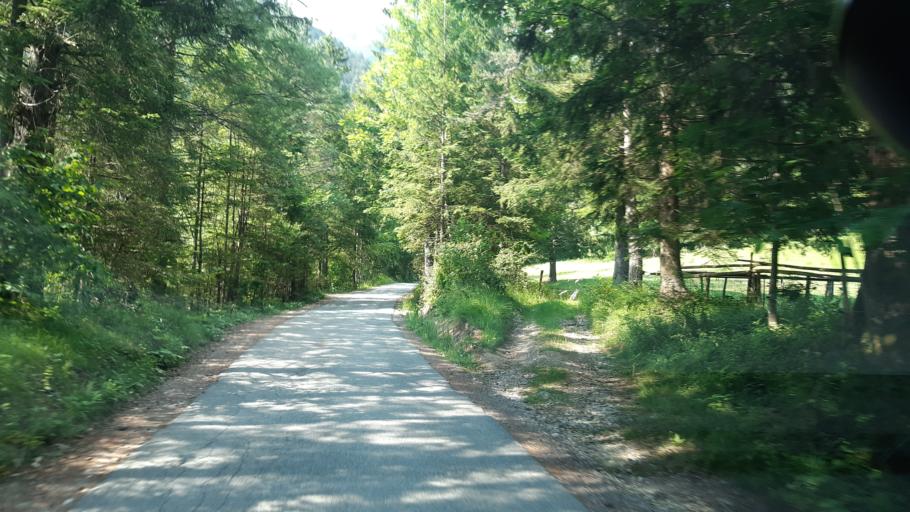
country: SI
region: Radovljica
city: Radovljica
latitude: 46.3923
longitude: 14.2180
